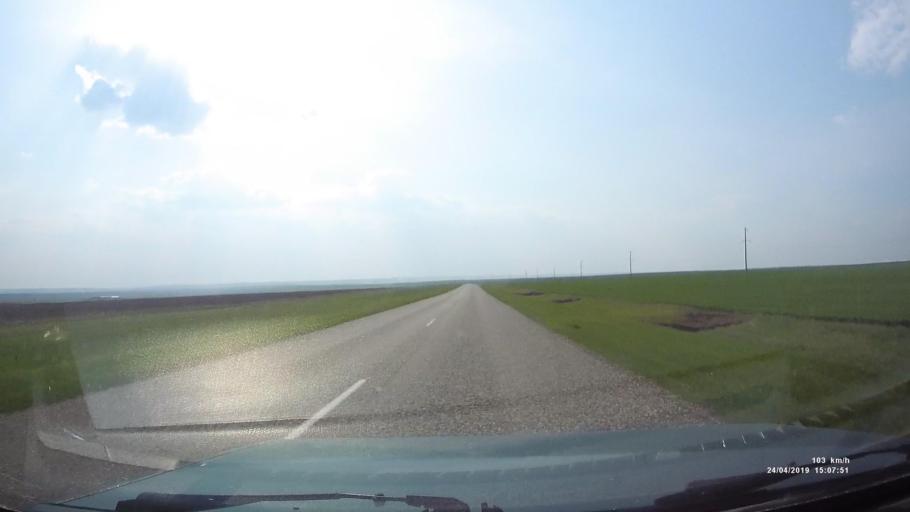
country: RU
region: Rostov
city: Remontnoye
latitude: 46.5599
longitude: 43.3959
